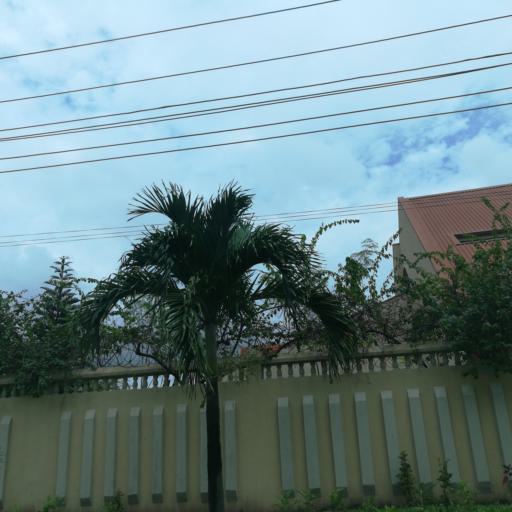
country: NG
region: Lagos
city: Ikoyi
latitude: 6.4439
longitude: 3.4608
